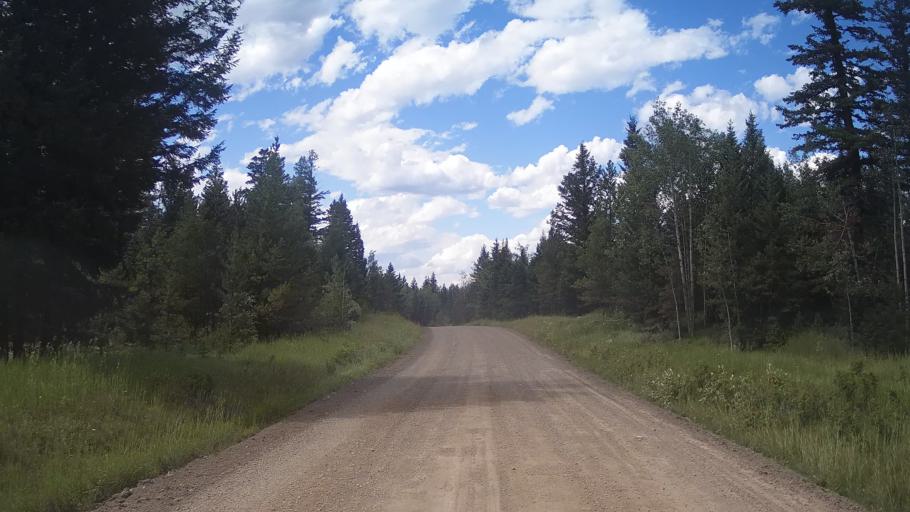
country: CA
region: British Columbia
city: Lillooet
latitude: 51.3228
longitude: -121.8682
